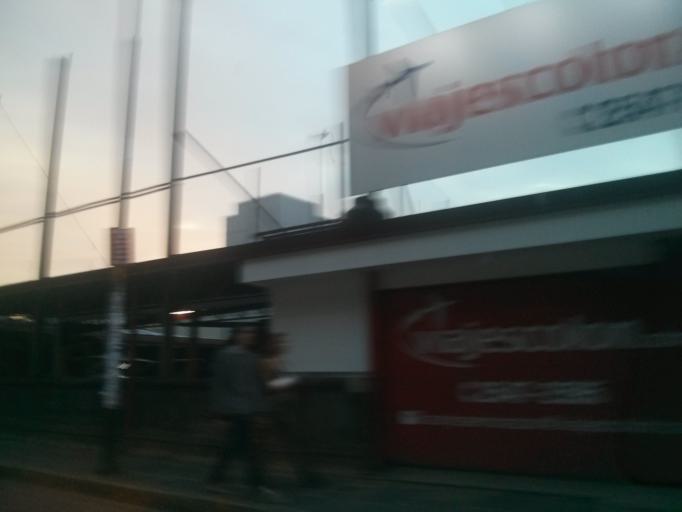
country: CR
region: San Jose
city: San Jose
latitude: 9.9346
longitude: -84.0763
